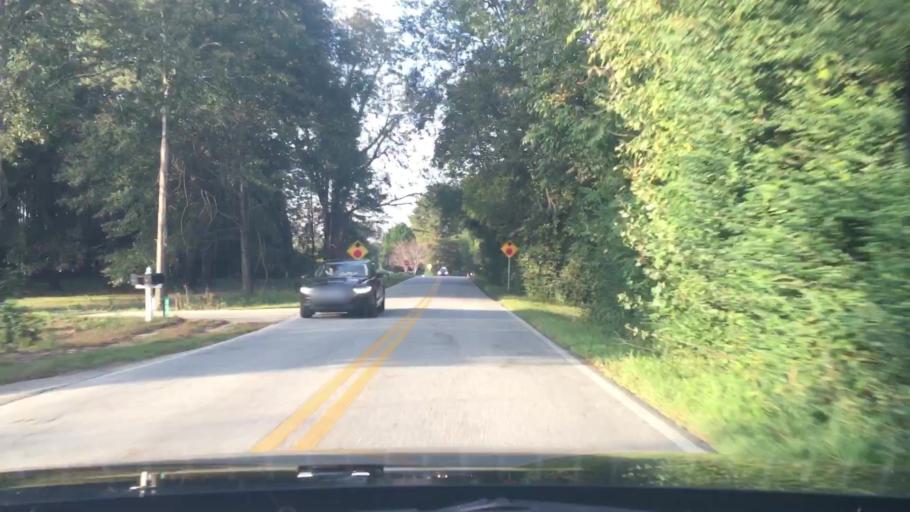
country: US
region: Georgia
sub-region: Coweta County
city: East Newnan
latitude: 33.3873
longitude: -84.7139
